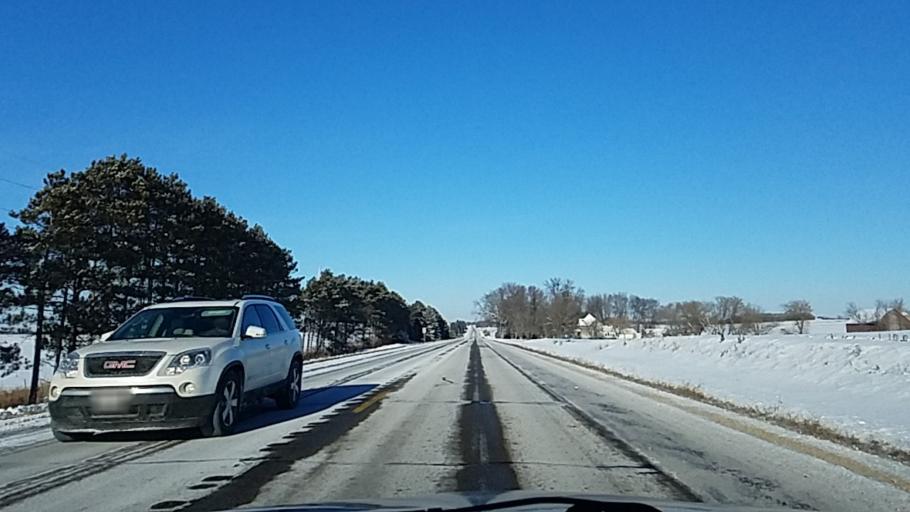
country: US
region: Wisconsin
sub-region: Saint Croix County
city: Roberts
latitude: 45.0370
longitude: -92.5374
